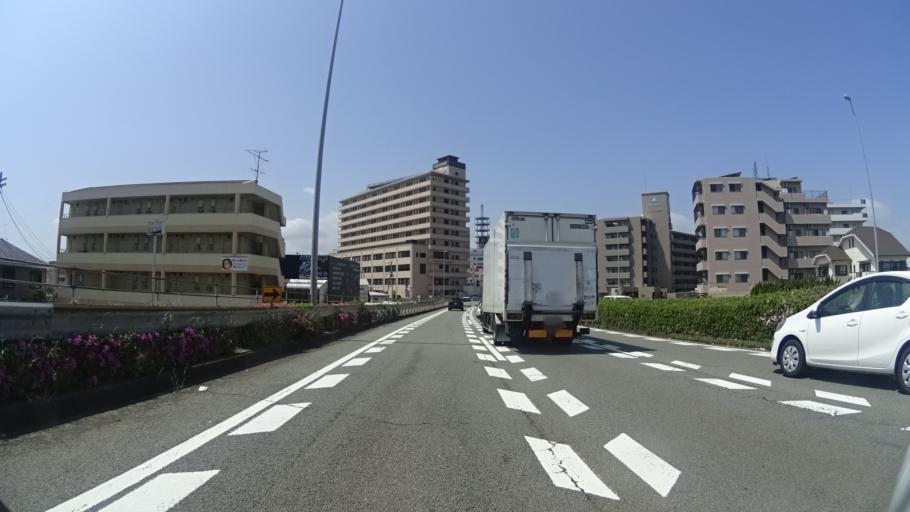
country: JP
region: Tokushima
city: Tokushima-shi
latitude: 34.0840
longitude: 134.5643
